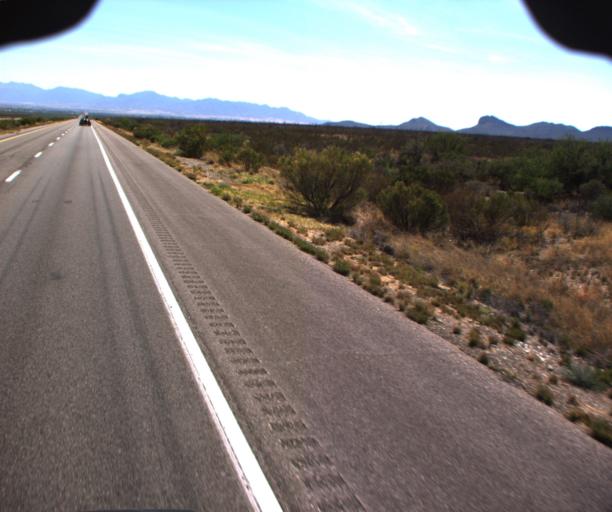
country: US
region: Arizona
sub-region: Cochise County
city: Huachuca City
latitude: 31.7762
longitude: -110.3503
